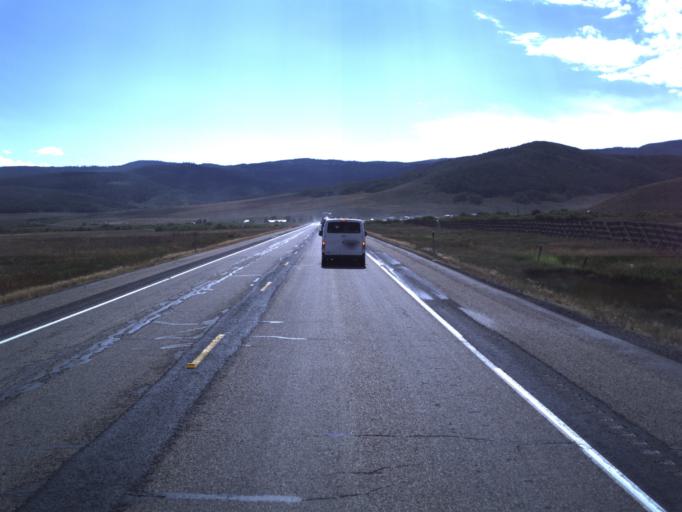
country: US
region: Utah
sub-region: Wasatch County
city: Heber
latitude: 40.2427
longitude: -111.1736
